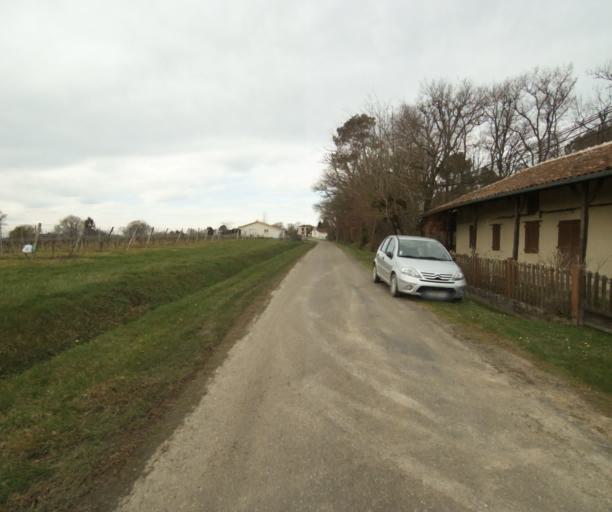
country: FR
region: Aquitaine
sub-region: Departement des Landes
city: Gabarret
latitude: 43.9416
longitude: 0.0186
